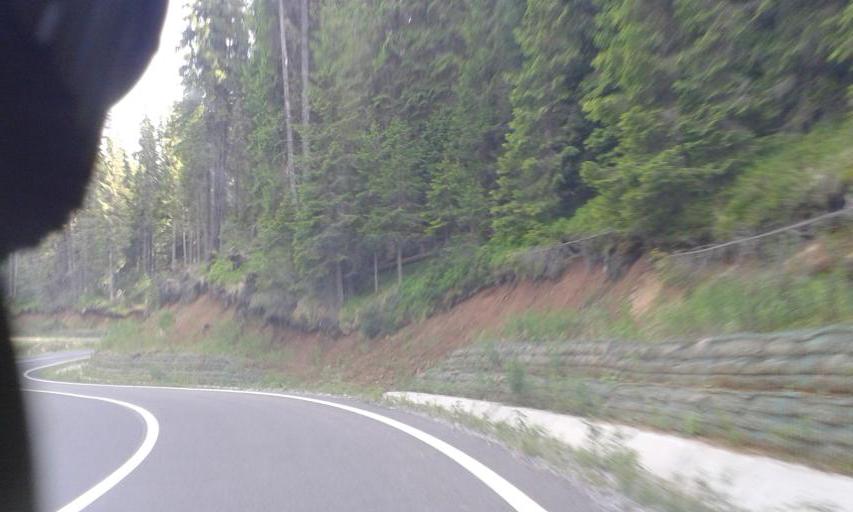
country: RO
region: Hunedoara
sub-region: Oras Petrila
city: Petrila
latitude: 45.5005
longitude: 23.6395
